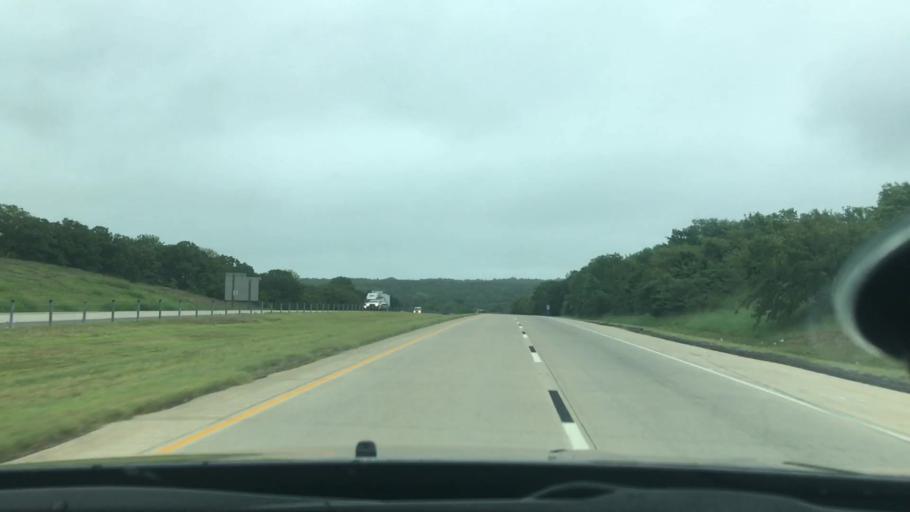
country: US
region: Oklahoma
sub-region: Okmulgee County
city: Henryetta
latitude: 35.4310
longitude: -95.9636
